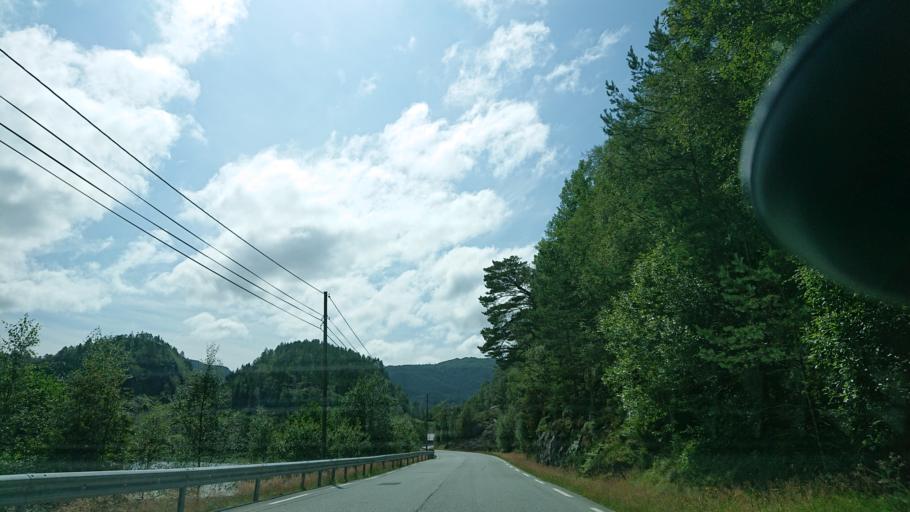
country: NO
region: Rogaland
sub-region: Hjelmeland
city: Hjelmelandsvagen
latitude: 59.2301
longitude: 6.2369
